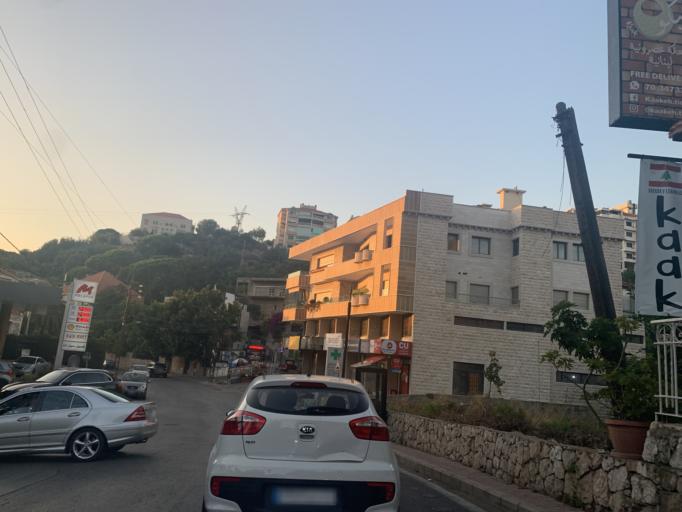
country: LB
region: Mont-Liban
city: Djounie
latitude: 33.9606
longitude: 35.6333
